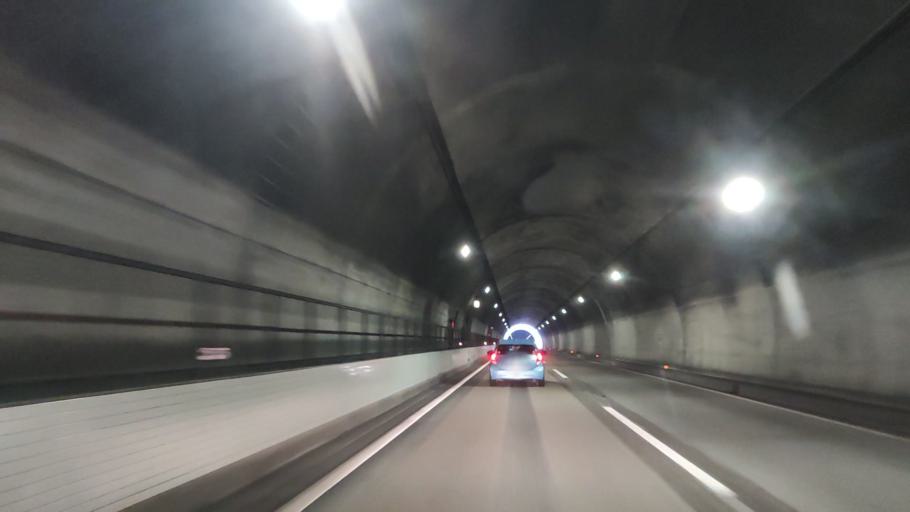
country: JP
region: Ehime
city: Saijo
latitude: 33.8741
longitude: 133.0741
